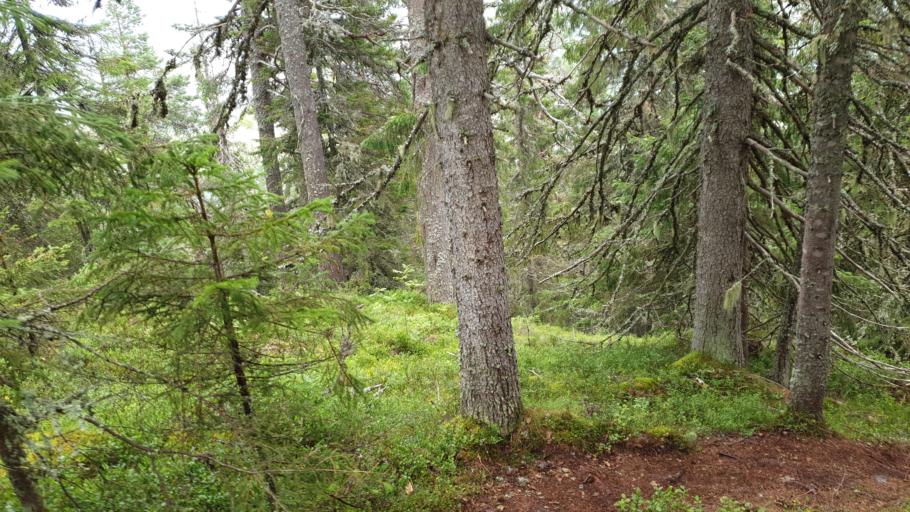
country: SE
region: Gaevleborg
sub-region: Hudiksvalls Kommun
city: Sorforsa
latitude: 61.6415
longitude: 16.7666
